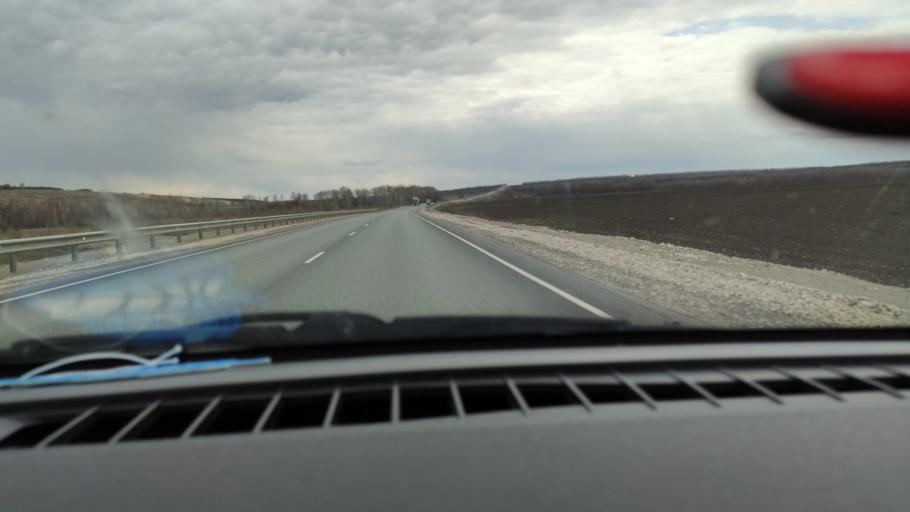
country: RU
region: Saratov
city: Yelshanka
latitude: 51.8544
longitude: 46.4922
